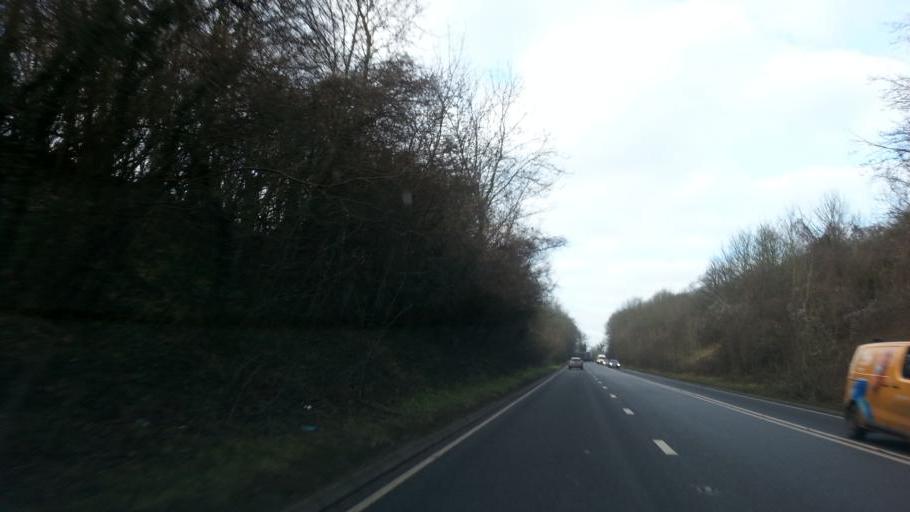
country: GB
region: England
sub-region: South Gloucestershire
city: Cold Ashton
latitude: 51.4181
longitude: -2.3511
